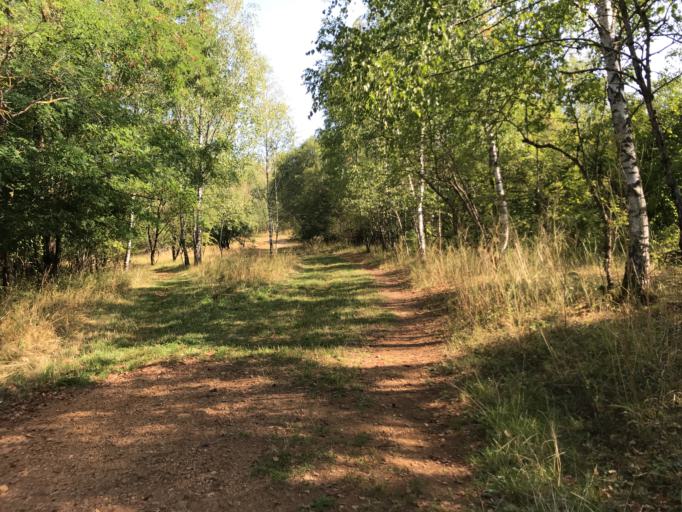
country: LU
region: Luxembourg
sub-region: Canton d'Esch-sur-Alzette
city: Petange
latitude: 49.5430
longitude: 5.8761
